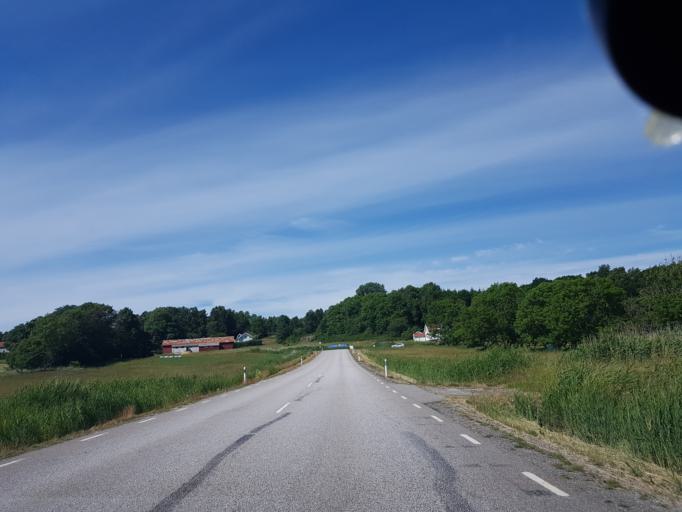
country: SE
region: Vaestra Goetaland
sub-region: Lysekils Kommun
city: Lysekil
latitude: 58.1544
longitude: 11.4643
